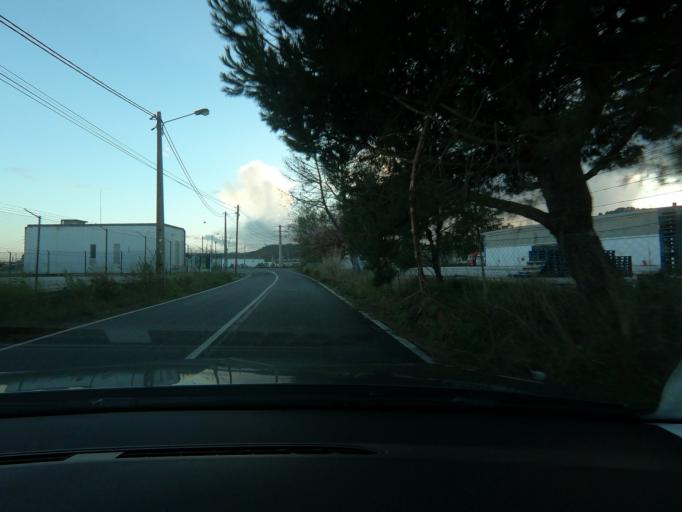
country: PT
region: Lisbon
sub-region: Vila Franca de Xira
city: Castanheira do Ribatejo
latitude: 38.9966
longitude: -8.9623
